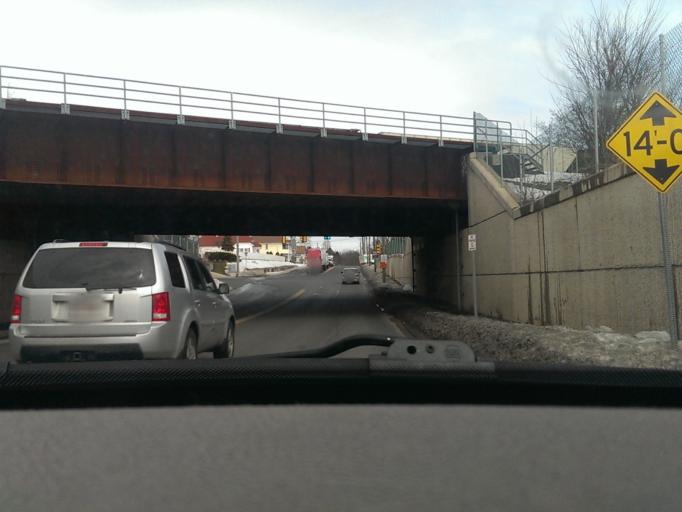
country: US
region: Massachusetts
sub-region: Hampden County
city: Ludlow
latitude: 42.1465
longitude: -72.4941
